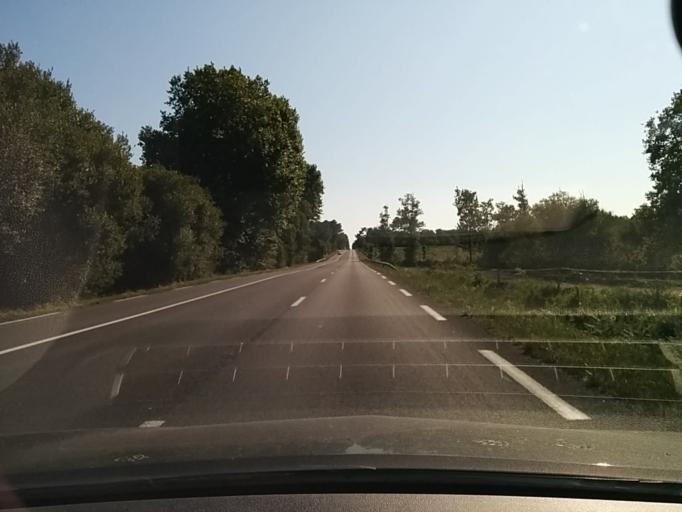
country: FR
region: Aquitaine
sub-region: Departement des Landes
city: Benesse-Maremne
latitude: 43.6457
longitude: -1.3344
